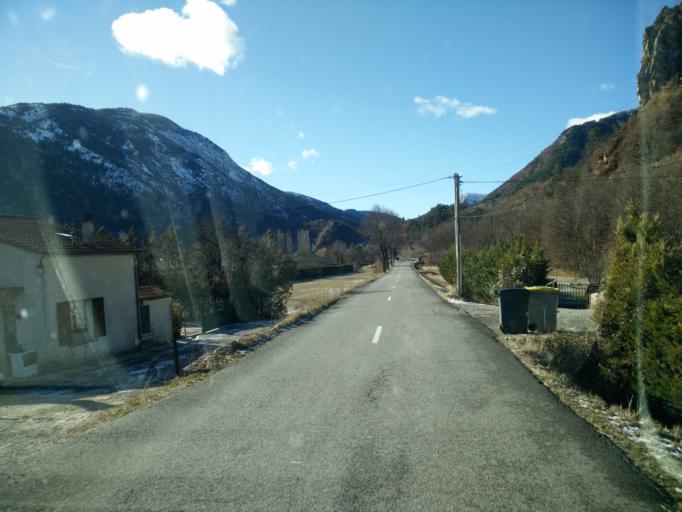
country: FR
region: Provence-Alpes-Cote d'Azur
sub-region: Departement des Alpes-de-Haute-Provence
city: Castellane
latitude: 43.8443
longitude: 6.5026
